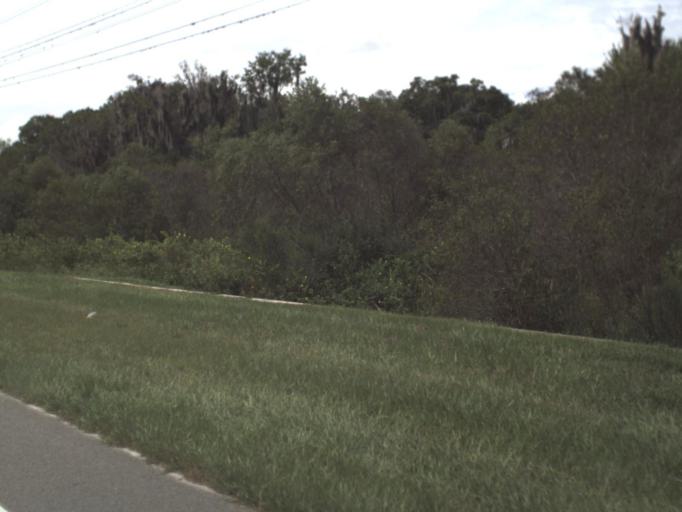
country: US
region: Florida
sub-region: Hillsborough County
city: Wimauma
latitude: 27.5902
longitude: -82.1273
